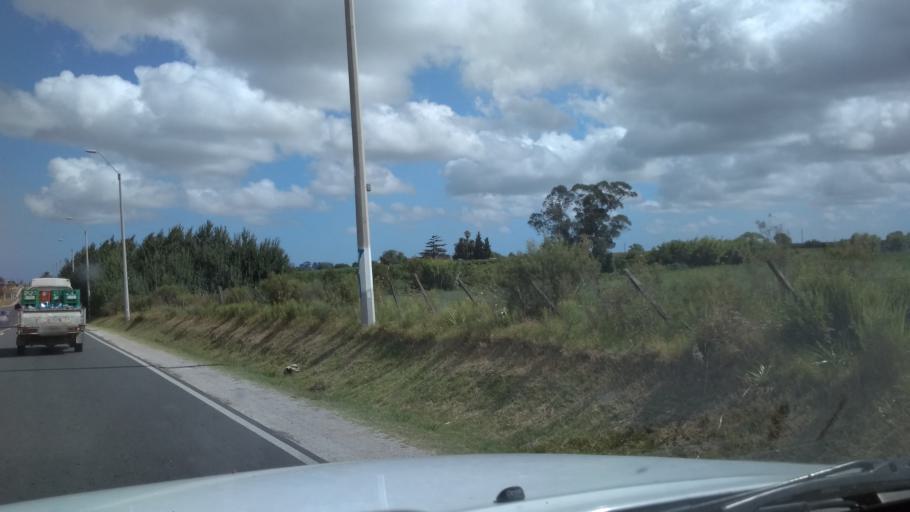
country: UY
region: Canelones
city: Joaquin Suarez
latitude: -34.7536
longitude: -56.0195
